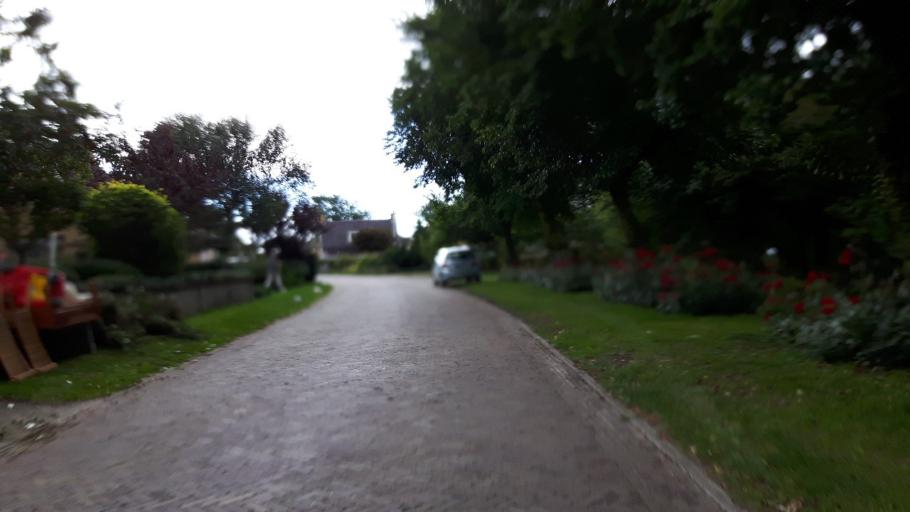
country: NL
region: Friesland
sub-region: Gemeente Ameland
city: Hollum
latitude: 53.4417
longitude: 5.6350
